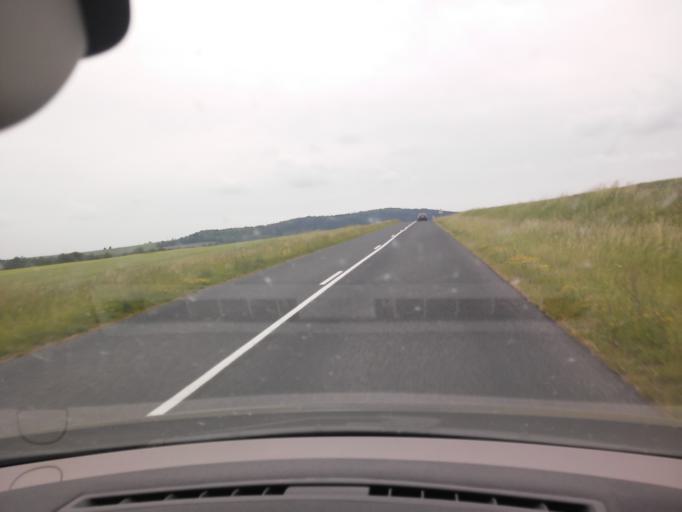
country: FR
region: Lorraine
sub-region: Departement de la Meuse
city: Saint-Mihiel
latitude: 48.8546
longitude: 5.5203
